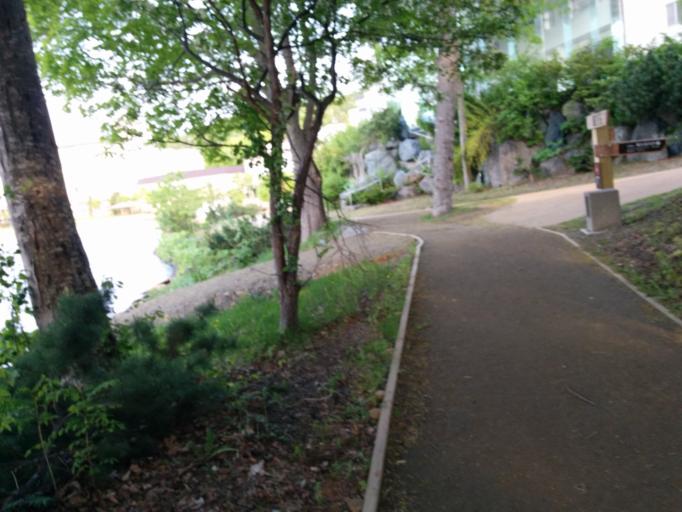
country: JP
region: Hokkaido
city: Bihoro
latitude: 43.4340
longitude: 144.0963
